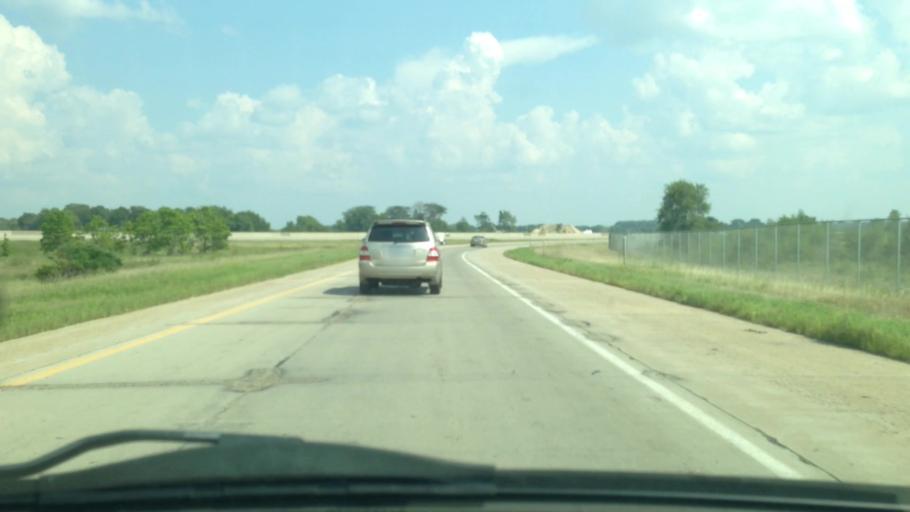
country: US
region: Iowa
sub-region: Black Hawk County
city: Cedar Falls
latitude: 42.5355
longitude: -92.3911
